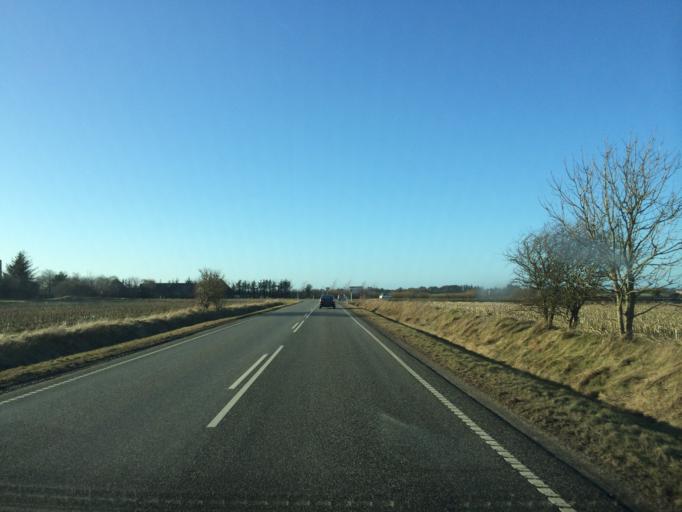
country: DK
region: Central Jutland
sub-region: Ringkobing-Skjern Kommune
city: Ringkobing
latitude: 56.1229
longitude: 8.2811
